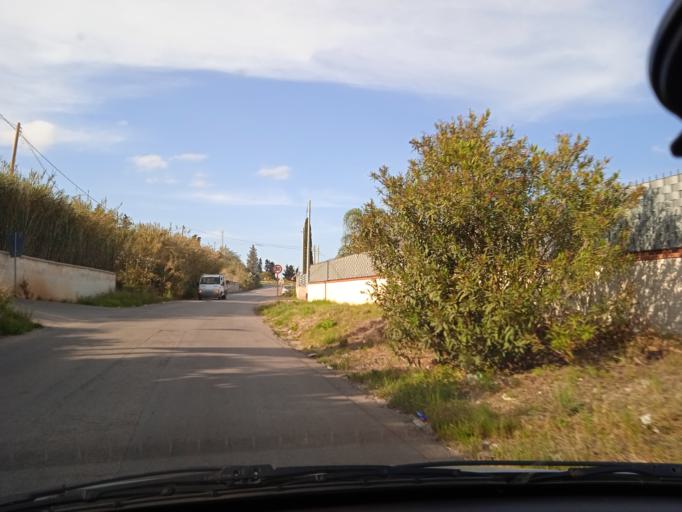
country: IT
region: Sicily
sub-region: Palermo
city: Portella di Mare
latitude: 38.0536
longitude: 13.4614
